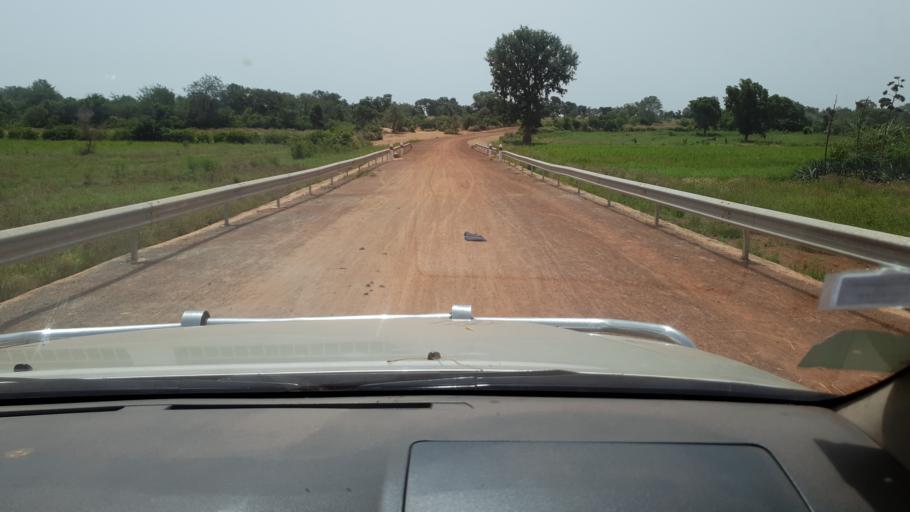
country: ML
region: Koulikoro
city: Kolokani
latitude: 13.4231
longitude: -8.2409
